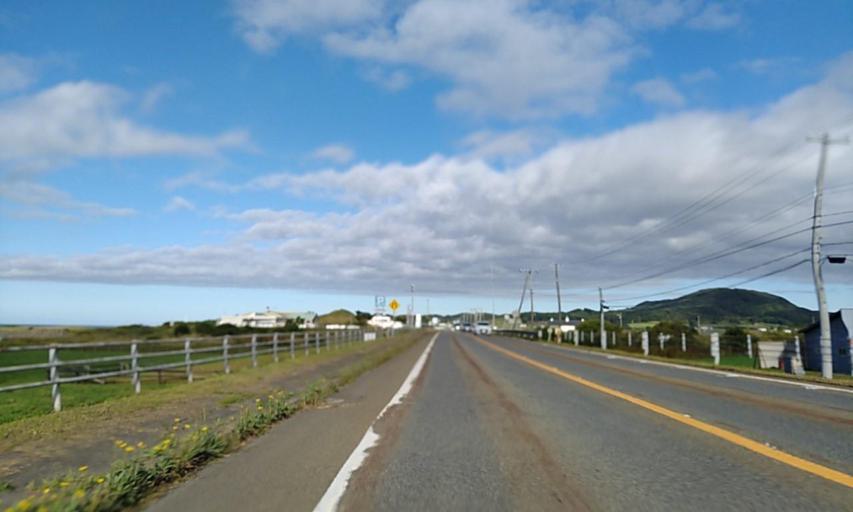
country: JP
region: Hokkaido
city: Shizunai-furukawacho
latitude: 42.2194
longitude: 142.6398
